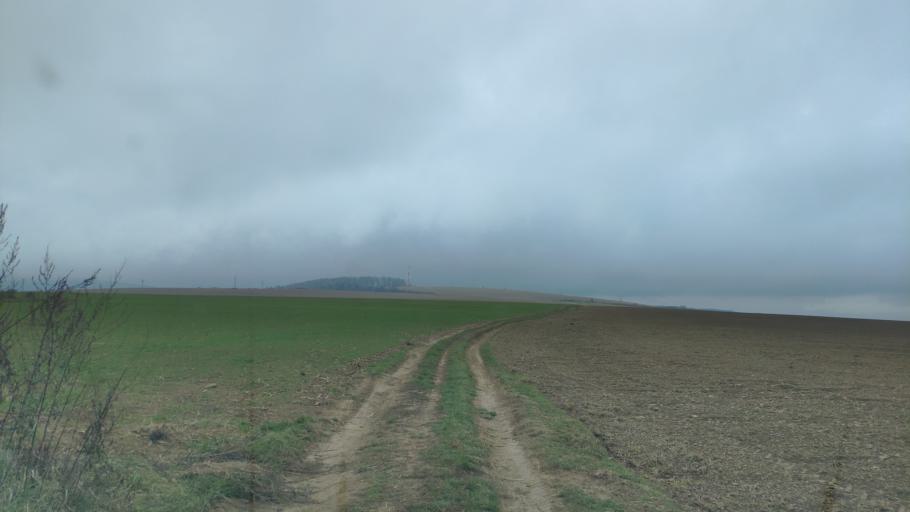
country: SK
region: Presovsky
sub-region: Okres Presov
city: Presov
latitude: 49.0132
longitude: 21.2103
